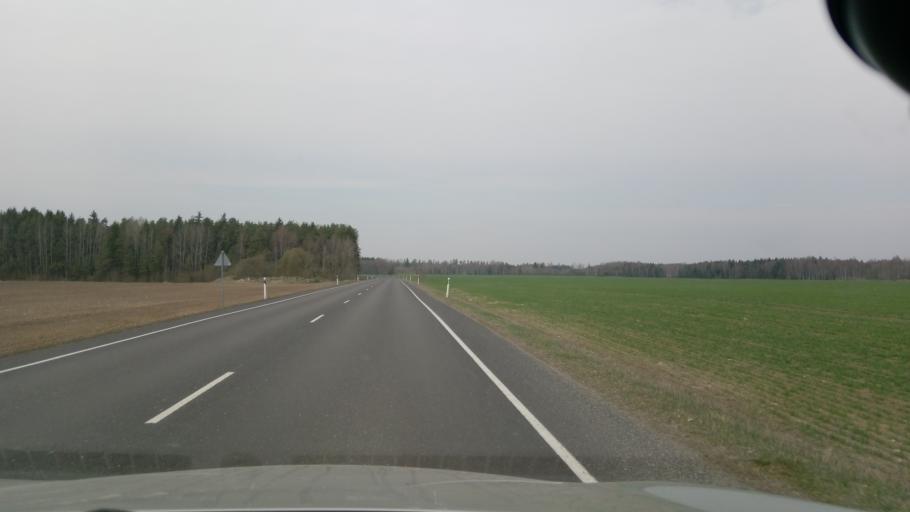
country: EE
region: Viljandimaa
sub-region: Vohma linn
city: Vohma
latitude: 58.7071
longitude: 25.6197
